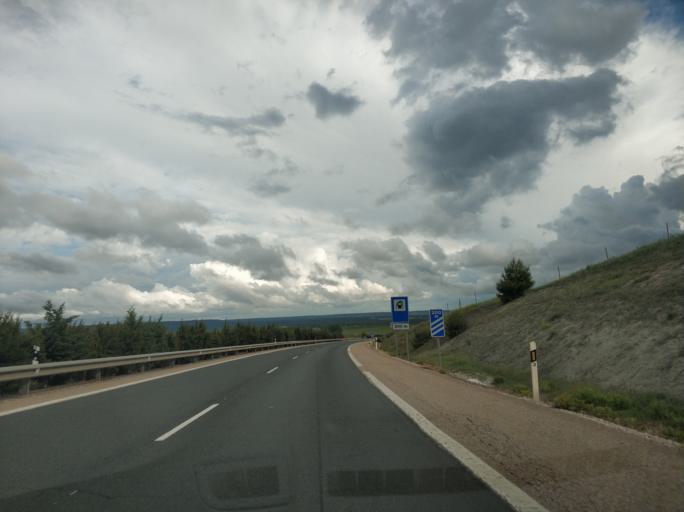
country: ES
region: Castille and Leon
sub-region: Provincia de Valladolid
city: Cisterniga
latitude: 41.6068
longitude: -4.6654
